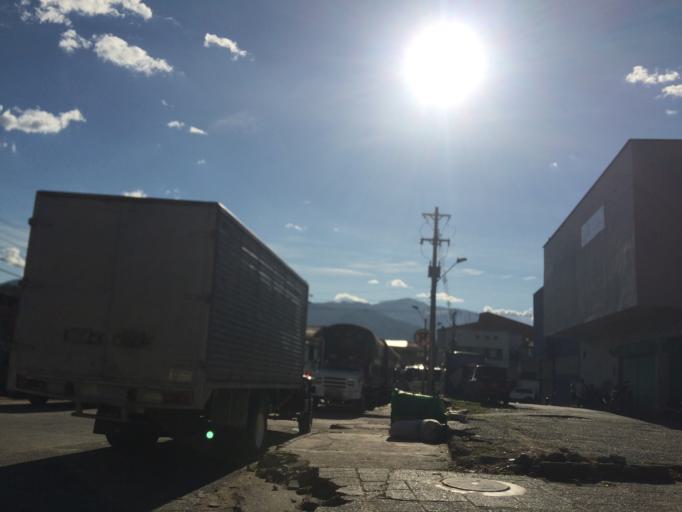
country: CO
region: Antioquia
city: Medellin
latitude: 6.2395
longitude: -75.5704
